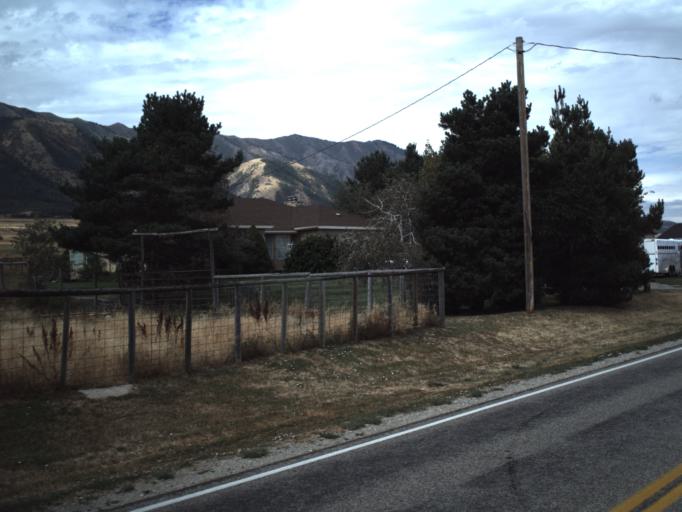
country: US
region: Utah
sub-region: Cache County
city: Wellsville
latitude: 41.6525
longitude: -111.9411
